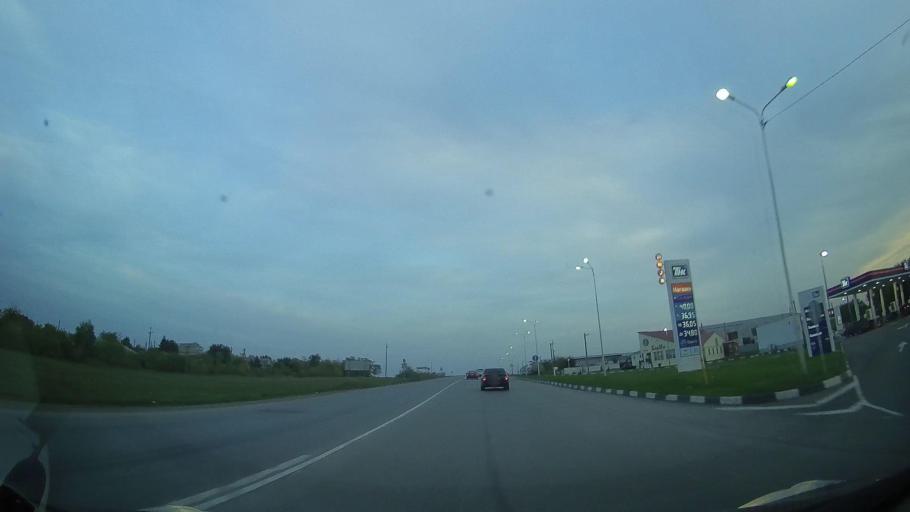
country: RU
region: Rostov
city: Kagal'nitskaya
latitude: 46.8768
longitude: 40.1577
